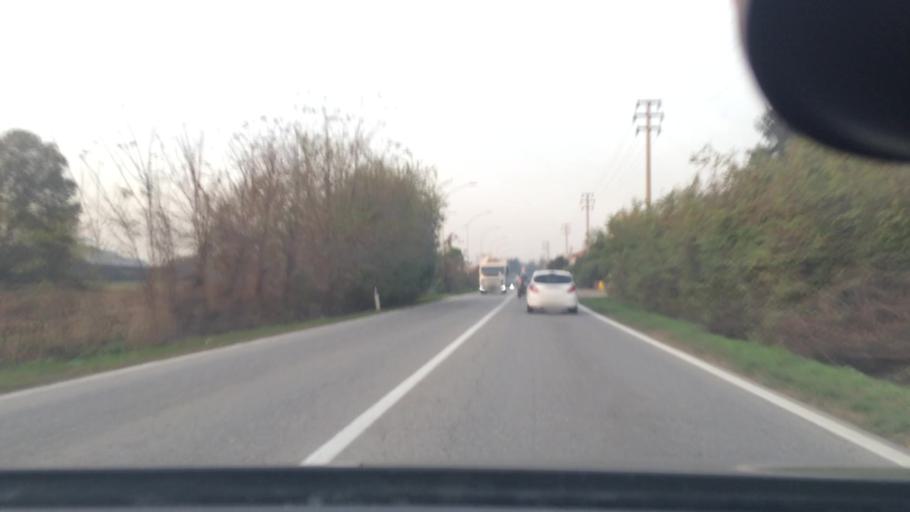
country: IT
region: Lombardy
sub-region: Provincia di Varese
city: Uboldo
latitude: 45.6139
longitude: 9.0202
